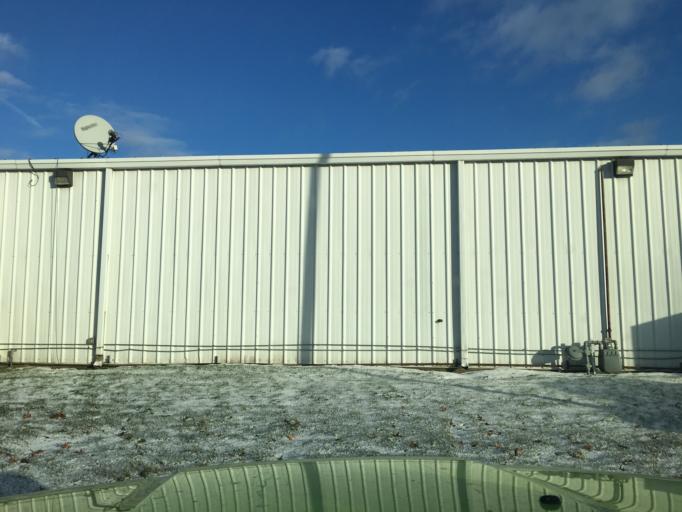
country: US
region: Michigan
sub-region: Montcalm County
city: Greenville
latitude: 43.2061
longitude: -85.2545
